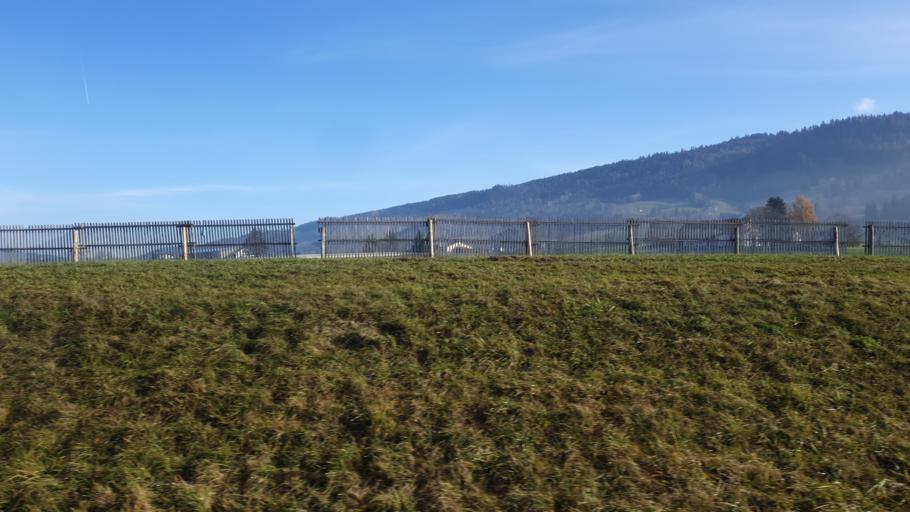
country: CH
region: Fribourg
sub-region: Veveyse District
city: Chatel-Saint-Denis
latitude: 46.5850
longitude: 6.9246
